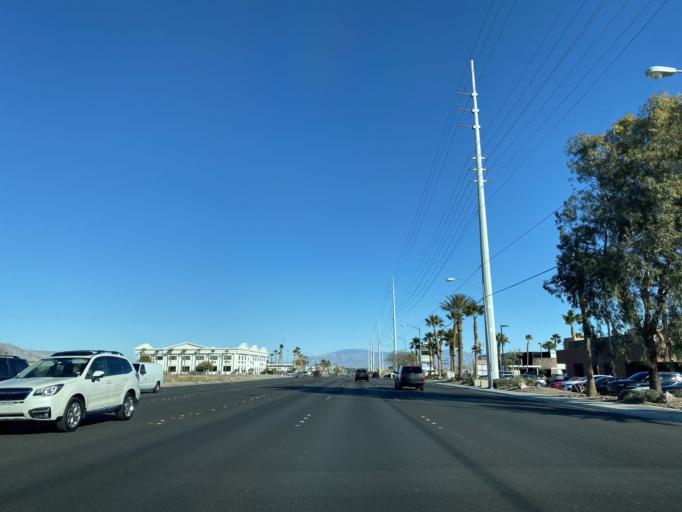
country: US
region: Nevada
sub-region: Clark County
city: Spring Valley
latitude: 36.0797
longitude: -115.2426
